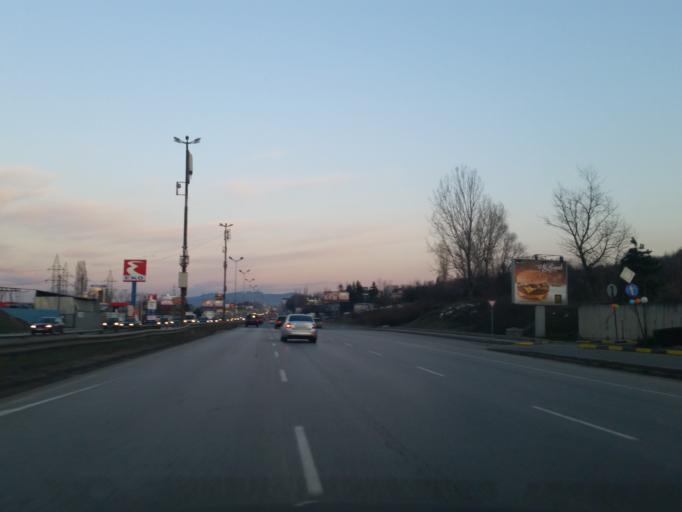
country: BG
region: Sofia-Capital
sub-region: Stolichna Obshtina
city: Sofia
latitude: 42.6506
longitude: 23.2906
